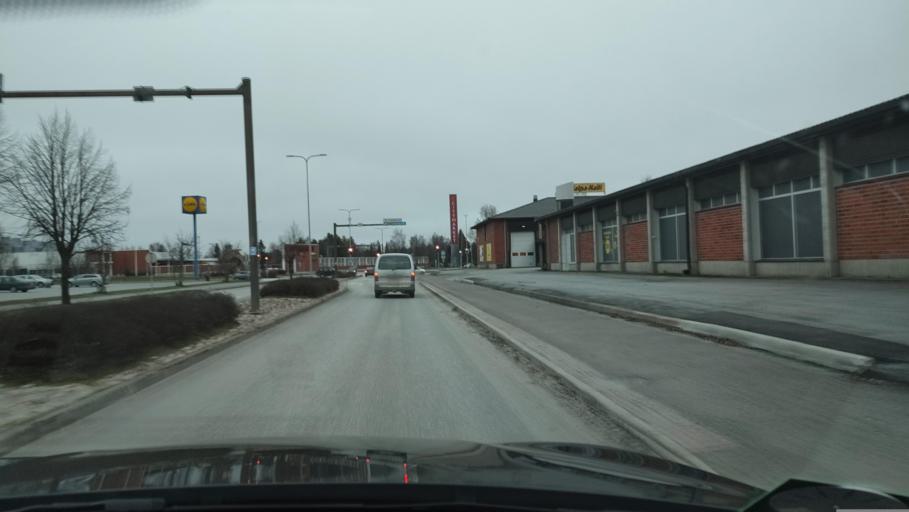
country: FI
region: Southern Ostrobothnia
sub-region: Suupohja
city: Kauhajoki
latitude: 62.4319
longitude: 22.1796
